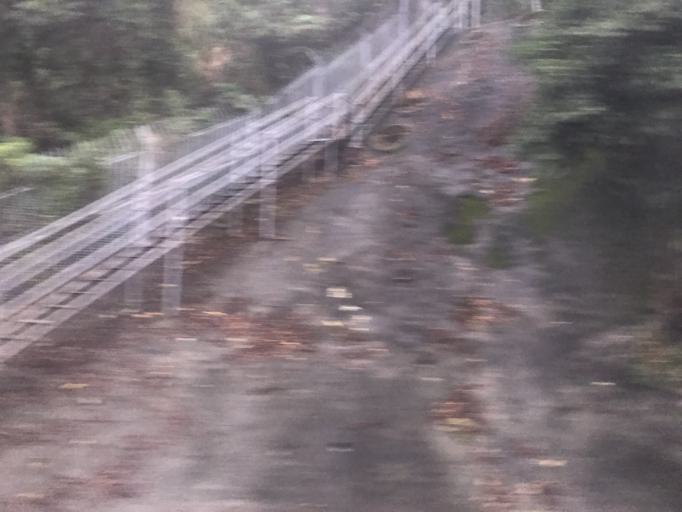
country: HK
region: Sha Tin
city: Sha Tin
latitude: 22.4090
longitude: 114.2110
